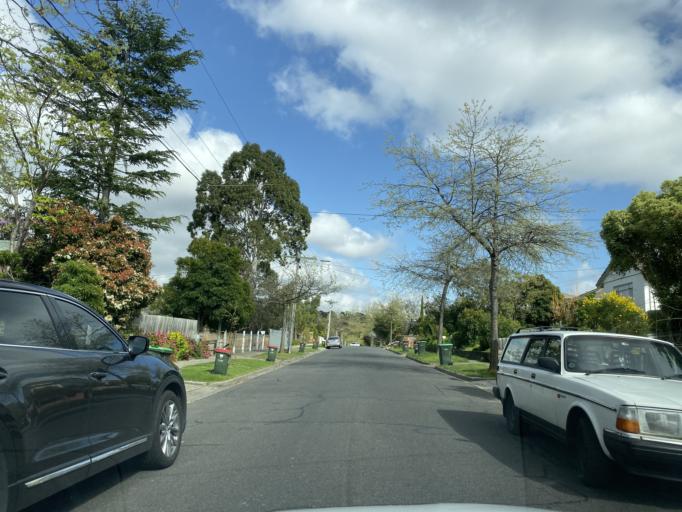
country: AU
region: Victoria
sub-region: Whitehorse
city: Burwood
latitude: -37.8421
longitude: 145.1153
